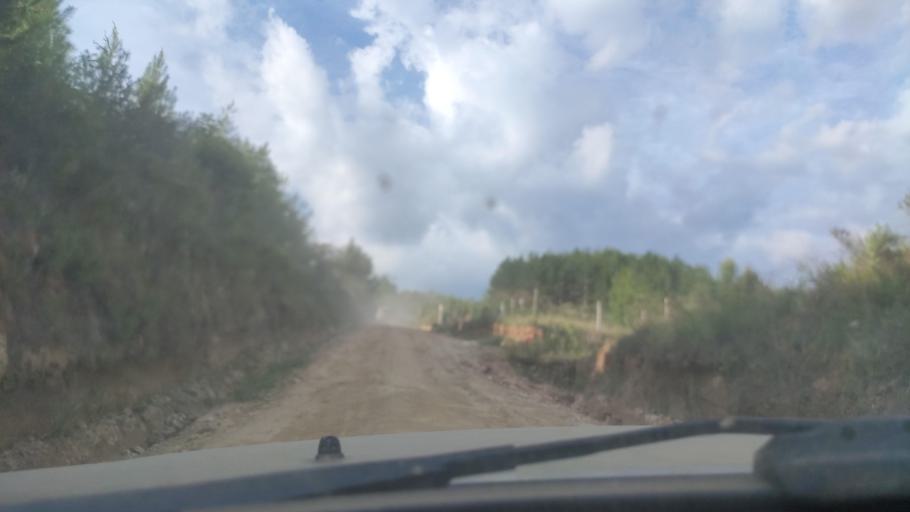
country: BR
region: Minas Gerais
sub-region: Camanducaia
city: Camanducaia
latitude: -22.7699
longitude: -45.9654
